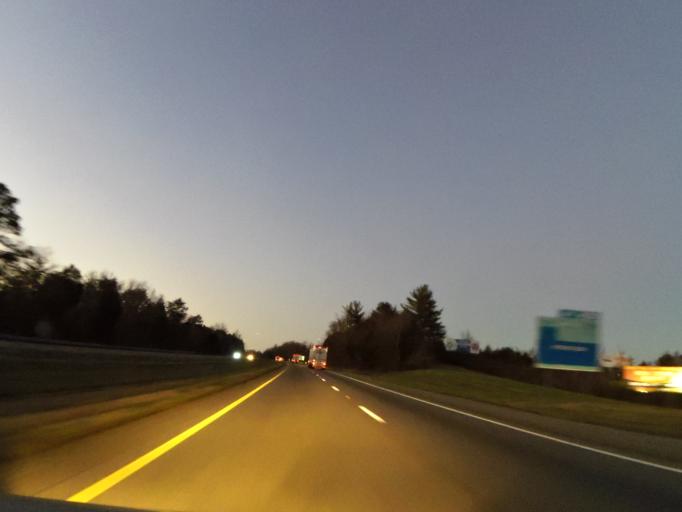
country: US
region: Tennessee
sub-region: Cocke County
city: Newport
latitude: 35.9226
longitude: -83.1890
